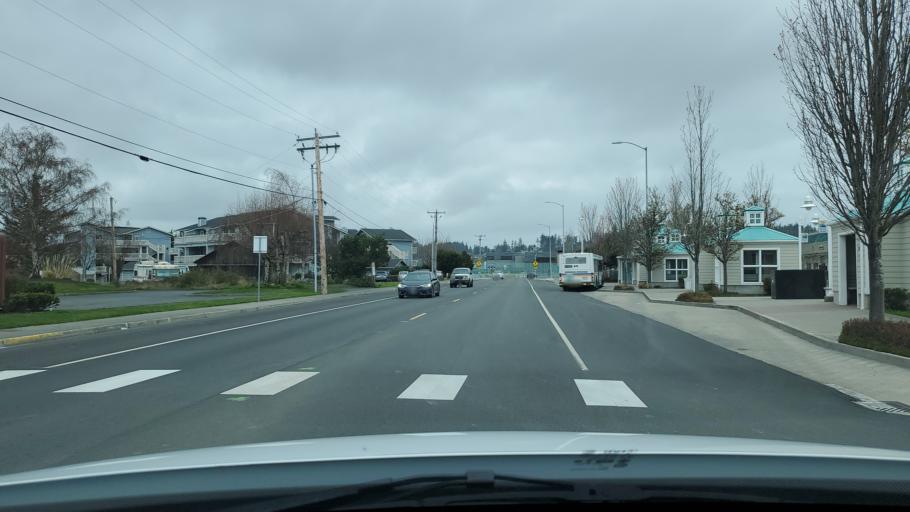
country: US
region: Washington
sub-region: Island County
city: Oak Harbor
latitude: 48.2876
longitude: -122.6481
